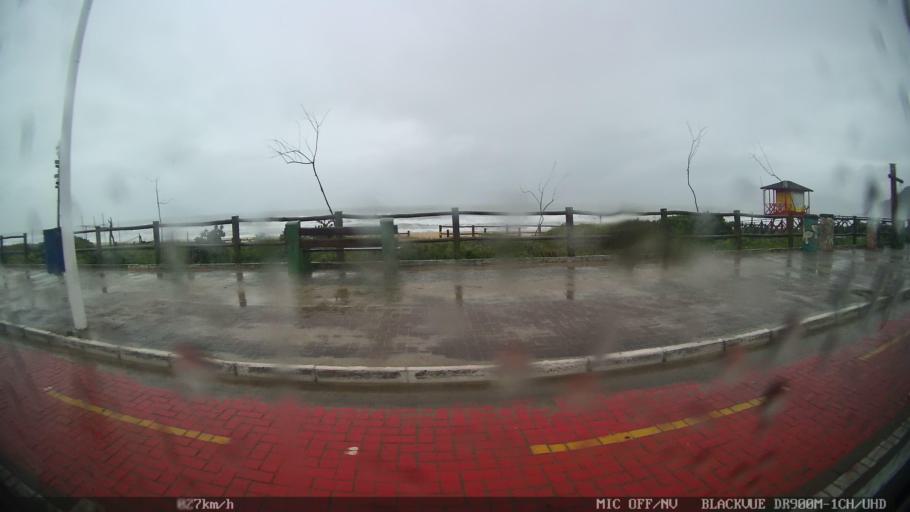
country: BR
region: Santa Catarina
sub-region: Balneario Camboriu
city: Balneario Camboriu
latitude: -26.9509
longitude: -48.6295
